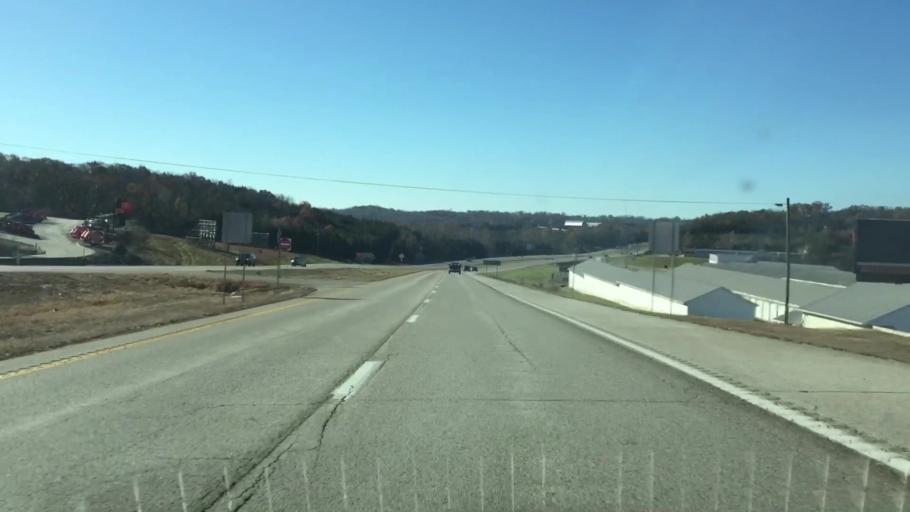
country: US
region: Missouri
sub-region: Cole County
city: Wardsville
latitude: 38.5321
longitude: -92.2193
